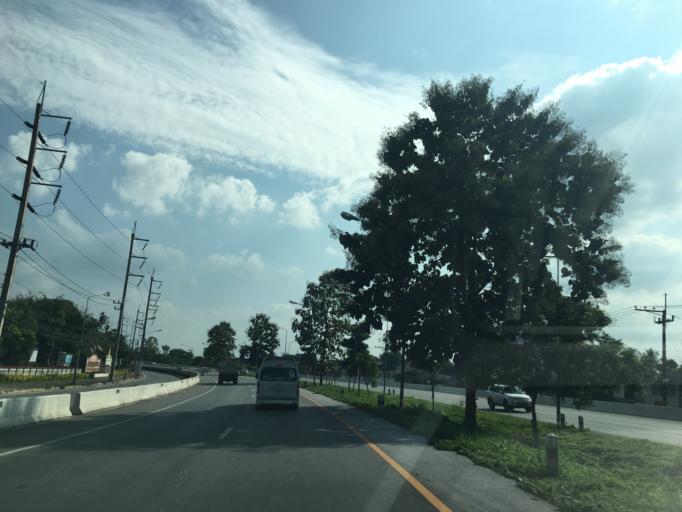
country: TH
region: Chiang Rai
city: Mae Lao
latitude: 19.7199
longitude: 99.7160
